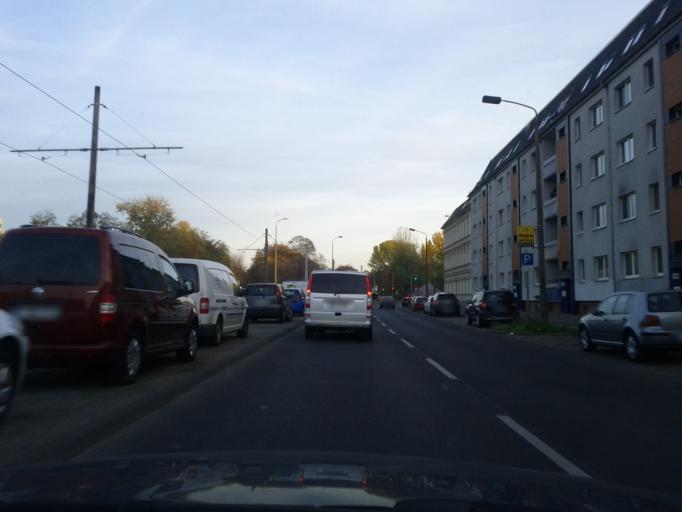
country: DE
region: Berlin
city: Berlin Koepenick
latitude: 52.4416
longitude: 13.5846
